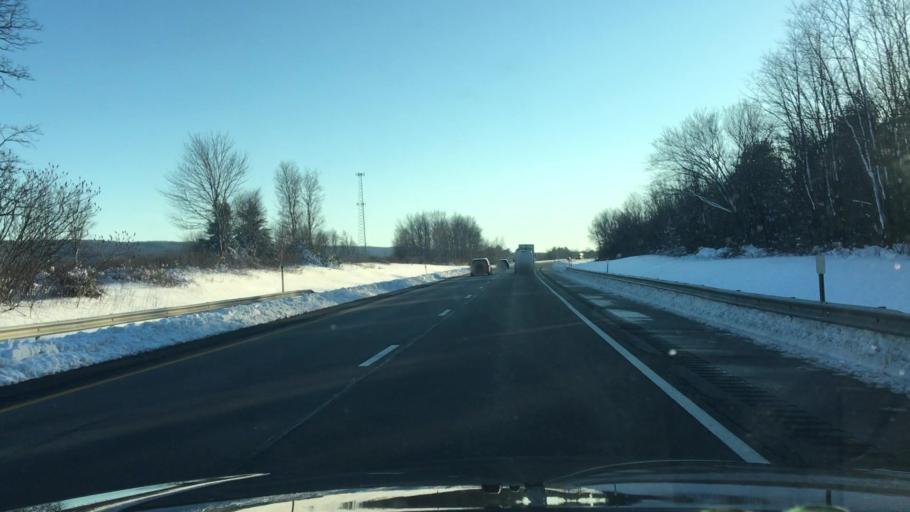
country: US
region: New York
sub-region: Chautauqua County
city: Westfield
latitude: 42.3189
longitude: -79.6137
